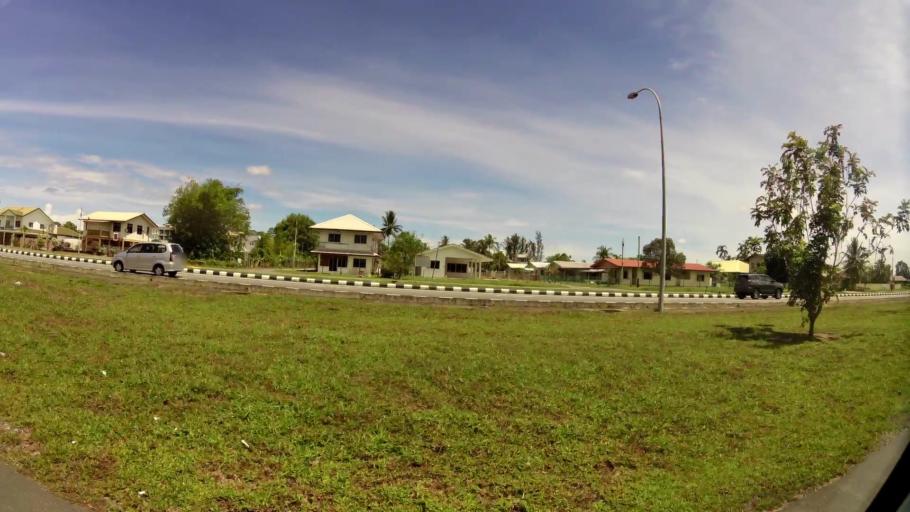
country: BN
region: Belait
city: Kuala Belait
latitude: 4.5939
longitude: 114.2363
